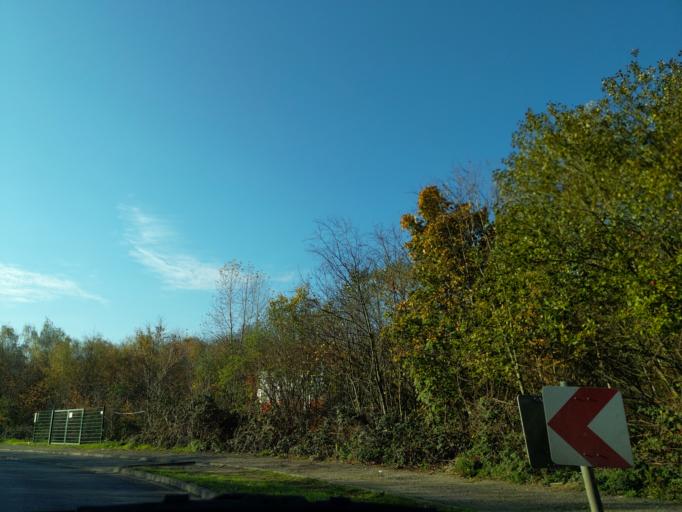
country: DE
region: North Rhine-Westphalia
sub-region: Regierungsbezirk Koln
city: Bilderstoeckchen
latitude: 51.0185
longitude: 6.9348
